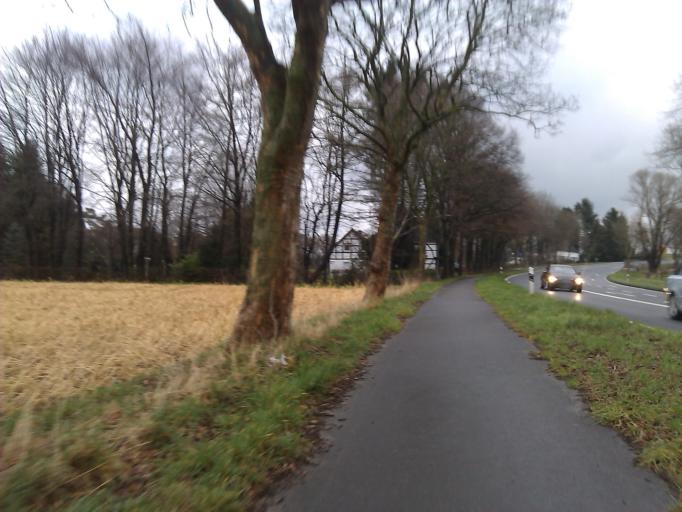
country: DE
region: North Rhine-Westphalia
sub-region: Regierungsbezirk Dusseldorf
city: Heiligenhaus
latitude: 51.3785
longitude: 6.9325
